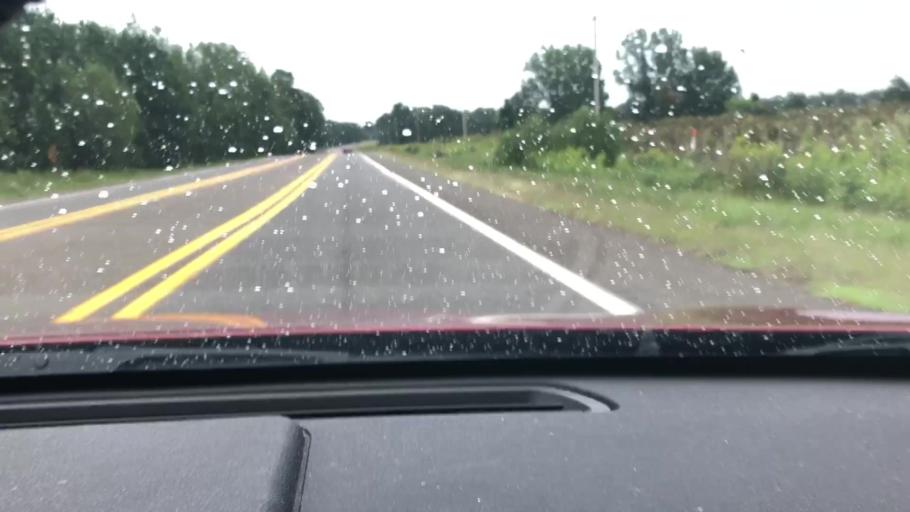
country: US
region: Arkansas
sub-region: Columbia County
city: Waldo
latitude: 33.3509
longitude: -93.3651
